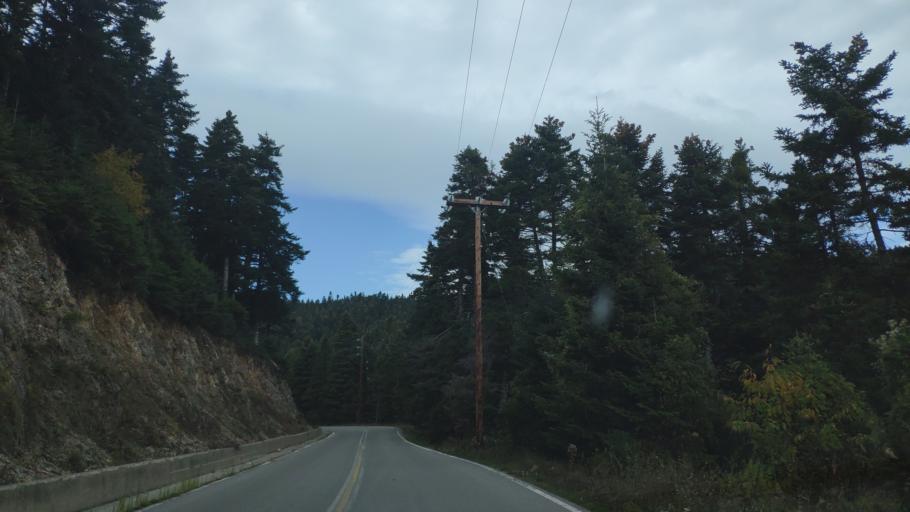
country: GR
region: Central Greece
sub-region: Nomos Fokidos
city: Amfissa
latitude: 38.7004
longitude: 22.3155
